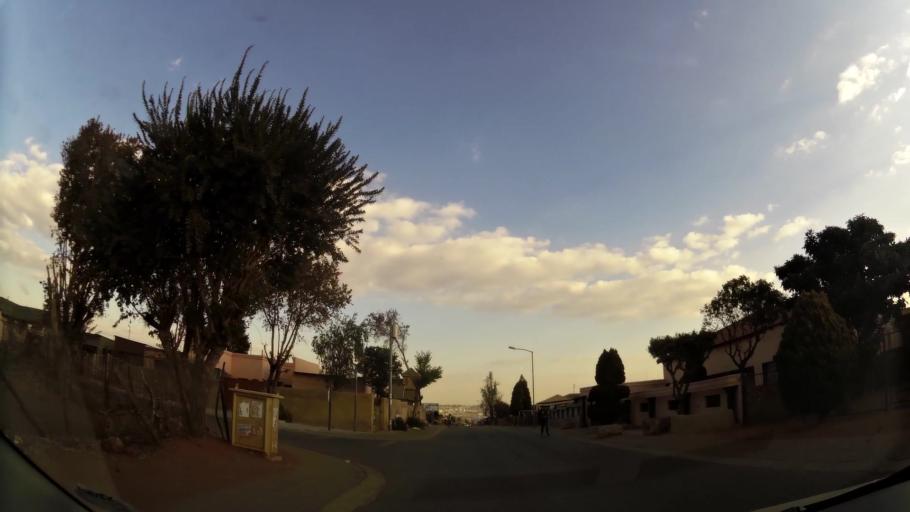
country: ZA
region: Gauteng
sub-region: West Rand District Municipality
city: Krugersdorp
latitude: -26.0731
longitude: 27.7586
